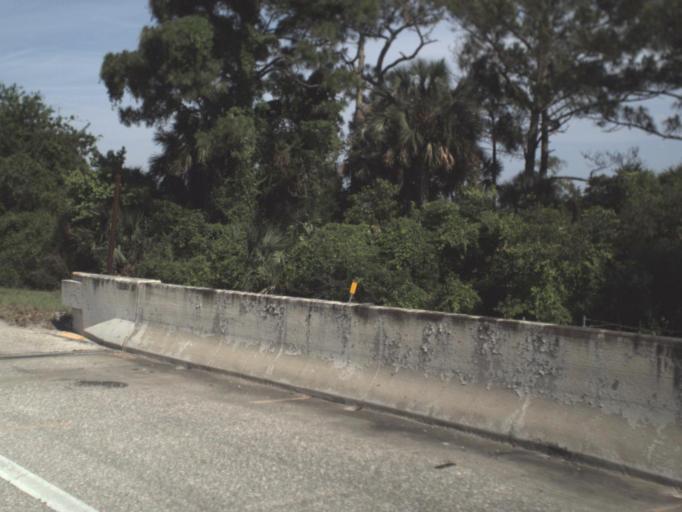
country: US
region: Florida
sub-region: Saint Johns County
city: Ponte Vedra Beach
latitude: 30.2580
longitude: -81.4174
